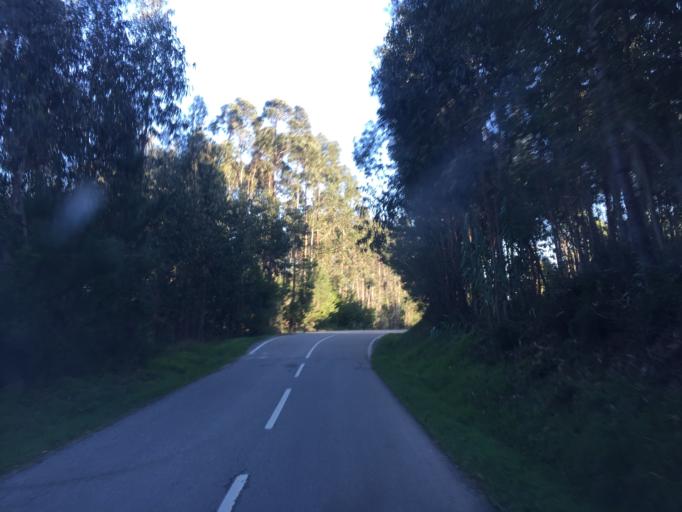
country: PT
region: Coimbra
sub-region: Figueira da Foz
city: Alhadas
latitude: 40.1576
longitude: -8.8000
